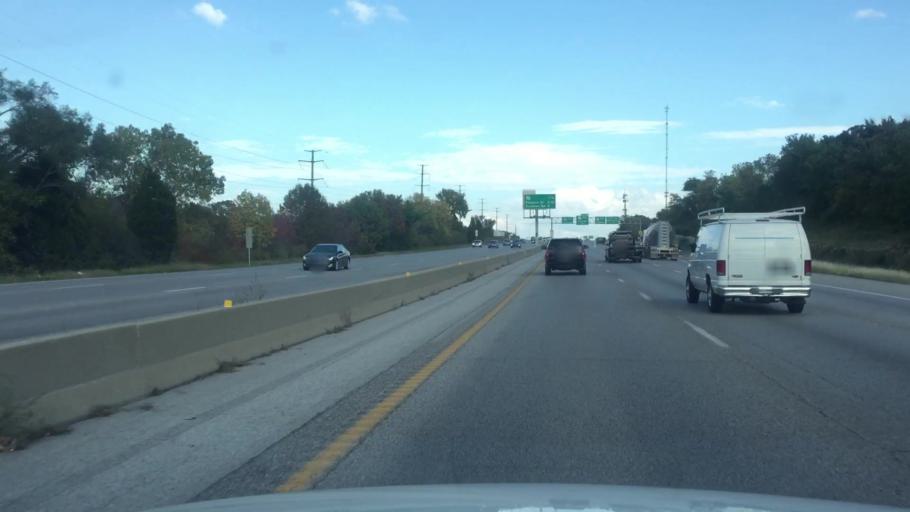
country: US
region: Missouri
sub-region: Jackson County
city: Lees Summit
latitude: 38.9349
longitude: -94.4288
